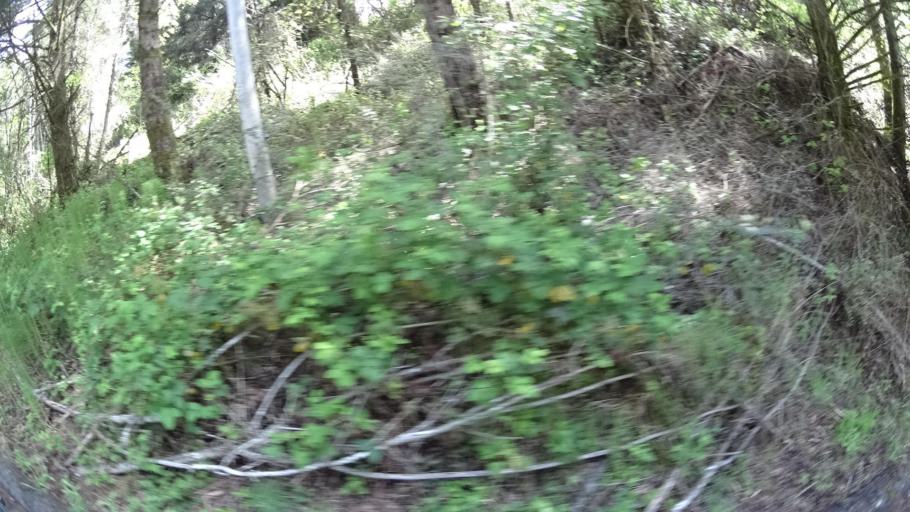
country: US
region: California
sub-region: Humboldt County
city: Arcata
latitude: 40.9091
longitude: -124.0448
